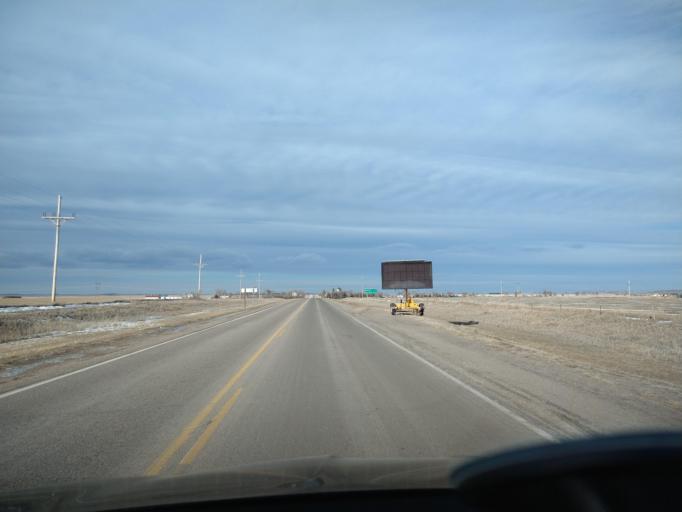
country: US
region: Nebraska
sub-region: Sheridan County
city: Rushville
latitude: 42.7187
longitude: -102.4785
